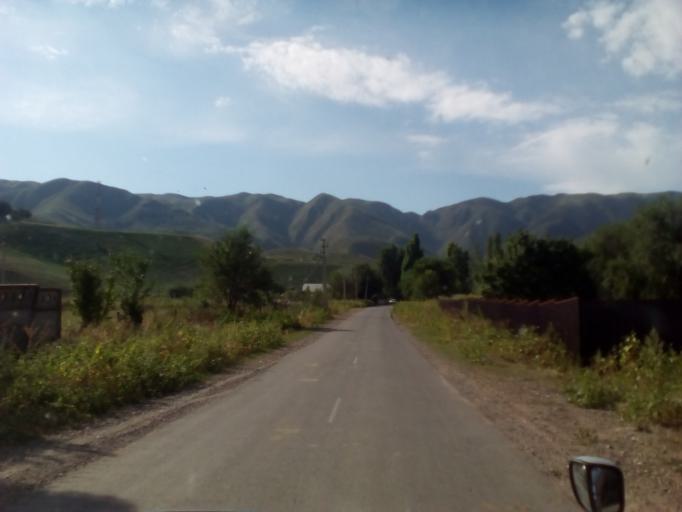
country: KZ
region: Almaty Oblysy
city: Burunday
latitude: 43.1563
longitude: 76.3846
